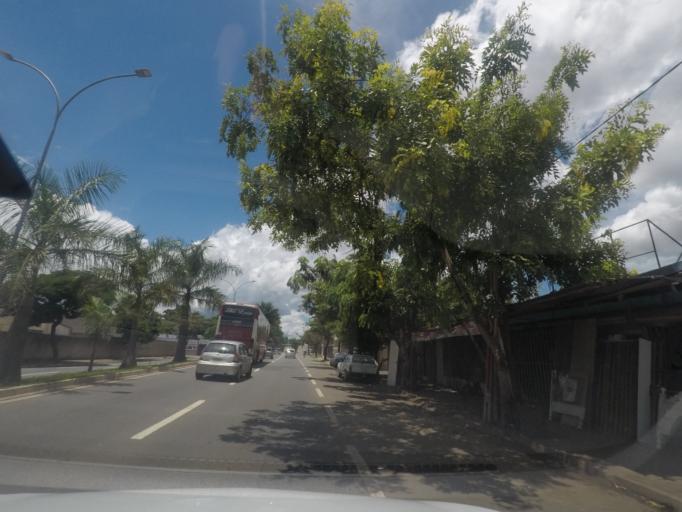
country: BR
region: Goias
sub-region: Goiania
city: Goiania
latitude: -16.6639
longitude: -49.2825
